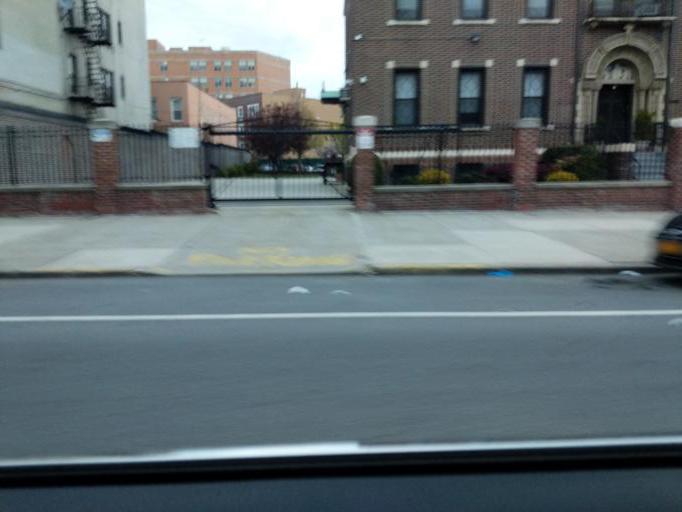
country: US
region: New York
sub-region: Bronx
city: The Bronx
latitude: 40.8415
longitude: -73.8531
